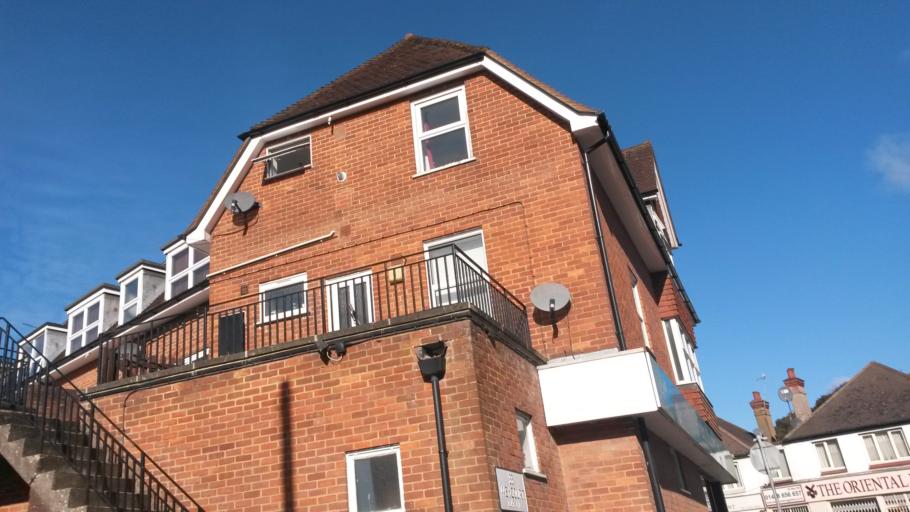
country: GB
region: England
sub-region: Surrey
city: Haslemere
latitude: 51.0875
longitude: -0.7286
